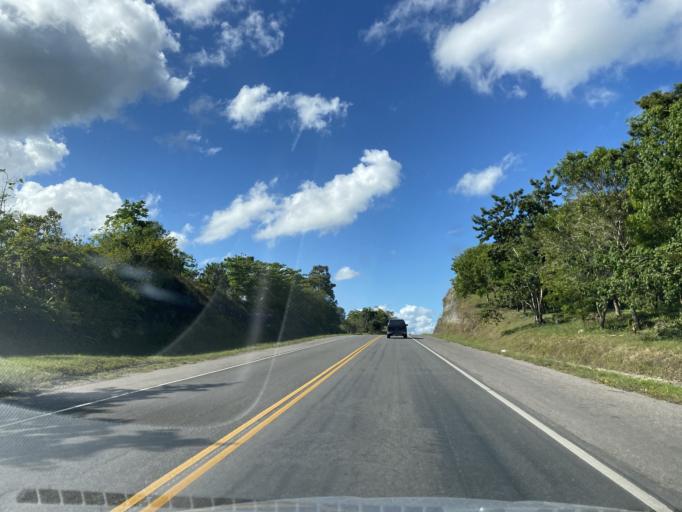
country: DO
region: Monte Plata
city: Gonzalo
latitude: 18.9669
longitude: -69.7721
